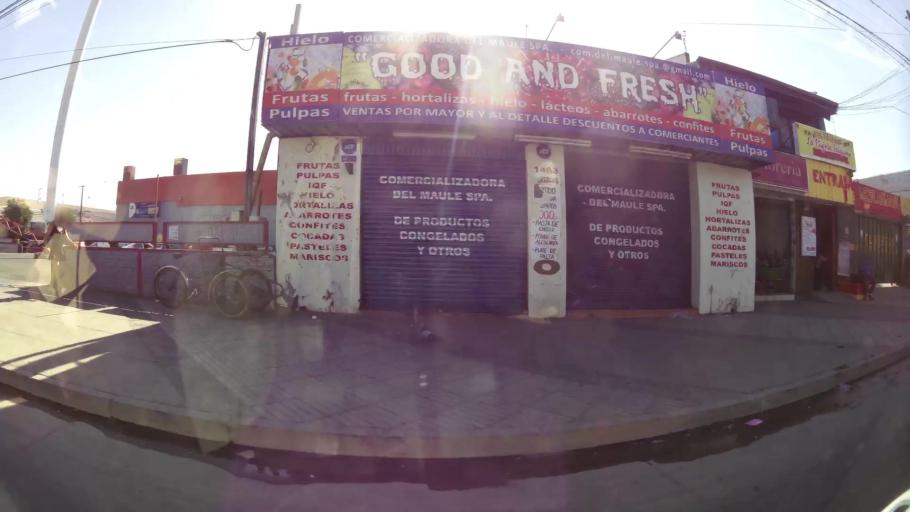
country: CL
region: Maule
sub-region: Provincia de Talca
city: Talca
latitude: -35.4240
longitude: -71.6499
